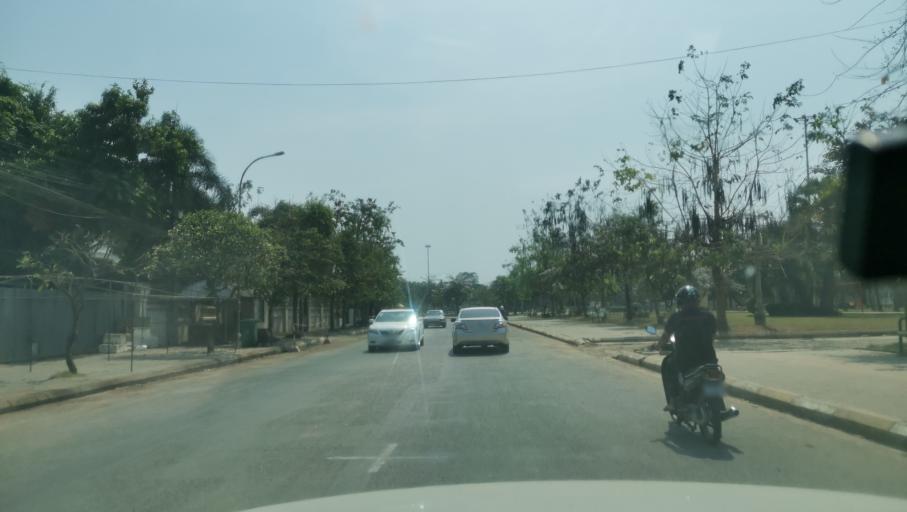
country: KH
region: Battambang
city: Battambang
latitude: 13.0959
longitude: 103.2001
